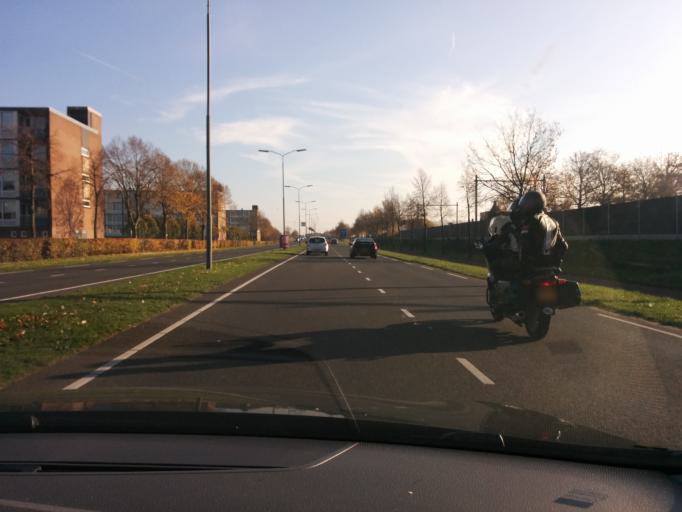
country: NL
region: North Brabant
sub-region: Gemeente Helmond
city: Helmond
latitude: 51.4739
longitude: 5.6840
